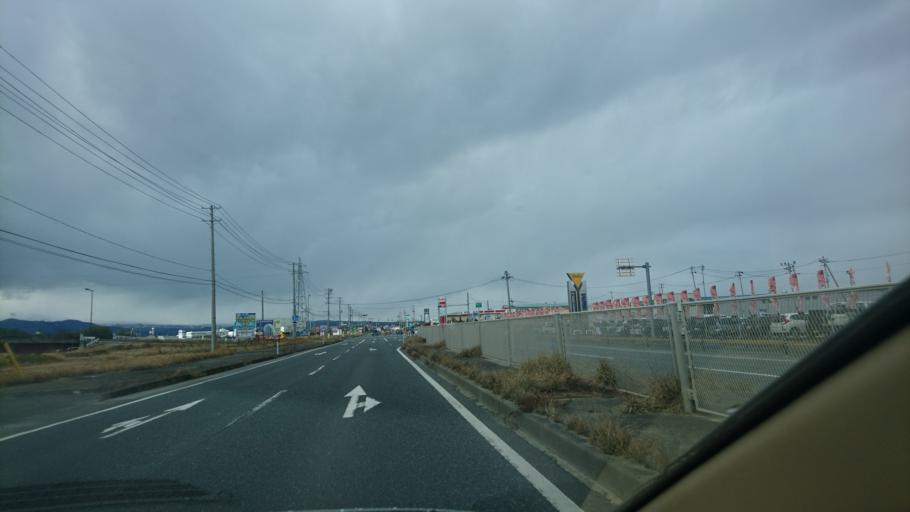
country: JP
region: Miyagi
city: Tomiya
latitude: 38.4358
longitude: 140.9110
